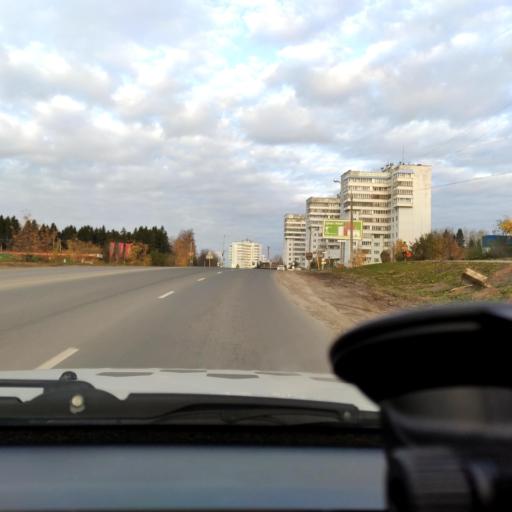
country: RU
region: Perm
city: Perm
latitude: 57.9629
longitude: 56.2004
